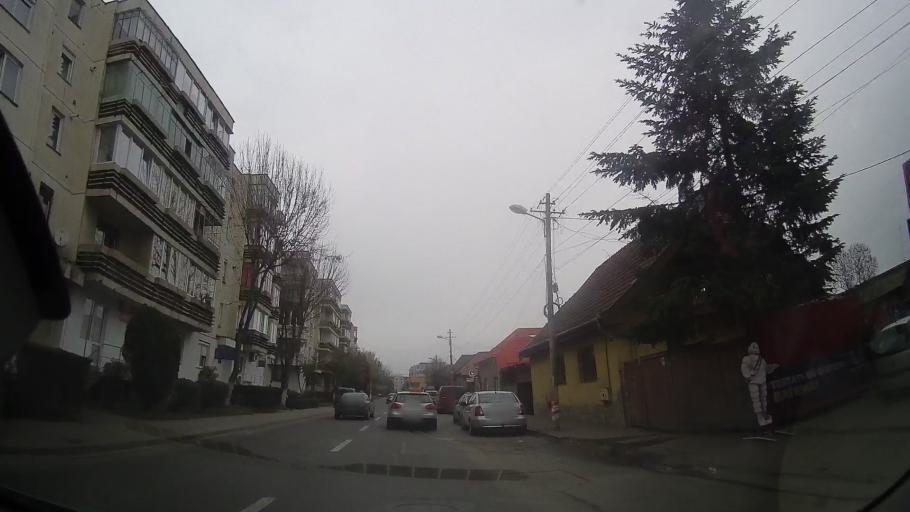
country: RO
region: Mures
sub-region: Comuna Santana de Mures
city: Santana de Mures
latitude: 46.5649
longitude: 24.5480
